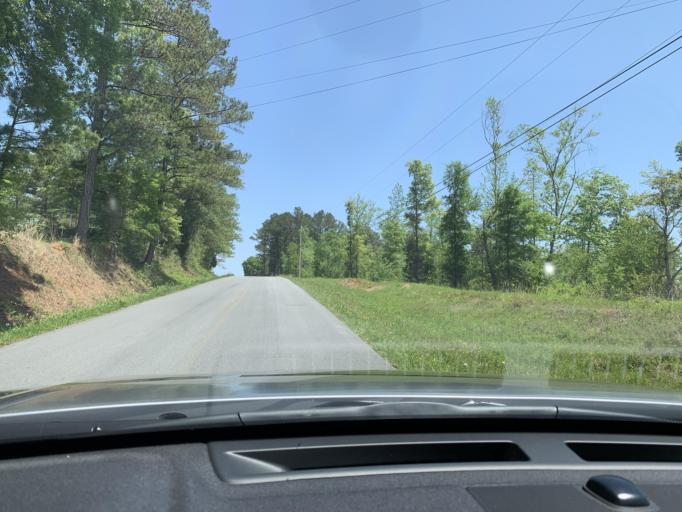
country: US
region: Georgia
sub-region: Polk County
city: Cedartown
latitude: 34.0435
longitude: -85.1883
